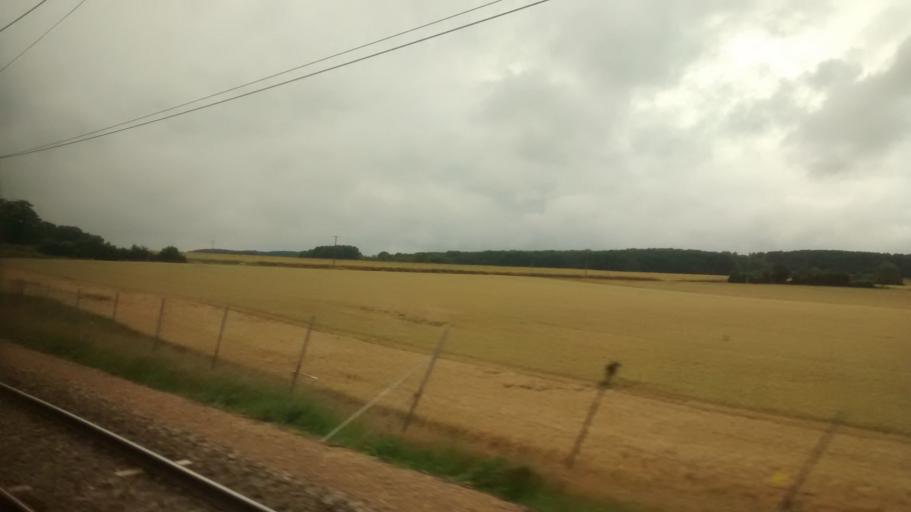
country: FR
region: Centre
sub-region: Departement d'Eure-et-Loir
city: La Bazoche-Gouet
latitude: 48.0855
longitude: 0.8972
